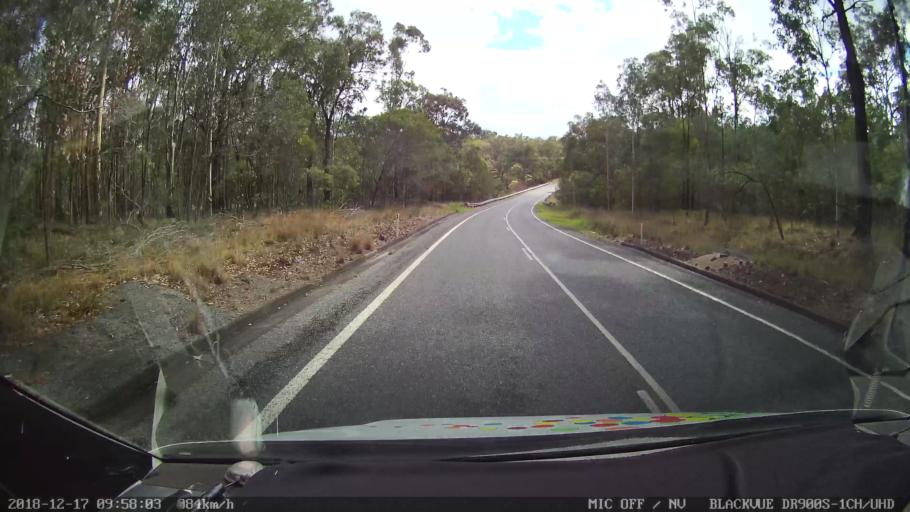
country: AU
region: New South Wales
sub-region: Tenterfield Municipality
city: Carrolls Creek
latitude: -28.9217
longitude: 152.4042
